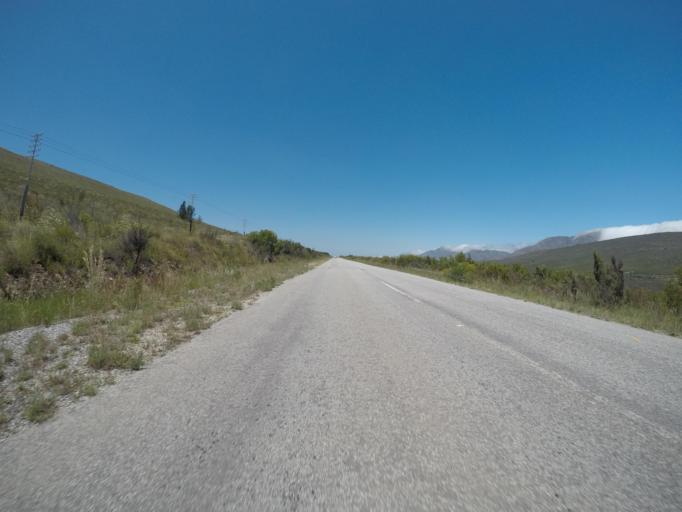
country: ZA
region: Eastern Cape
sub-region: Cacadu District Municipality
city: Kareedouw
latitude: -33.8464
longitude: 23.9538
